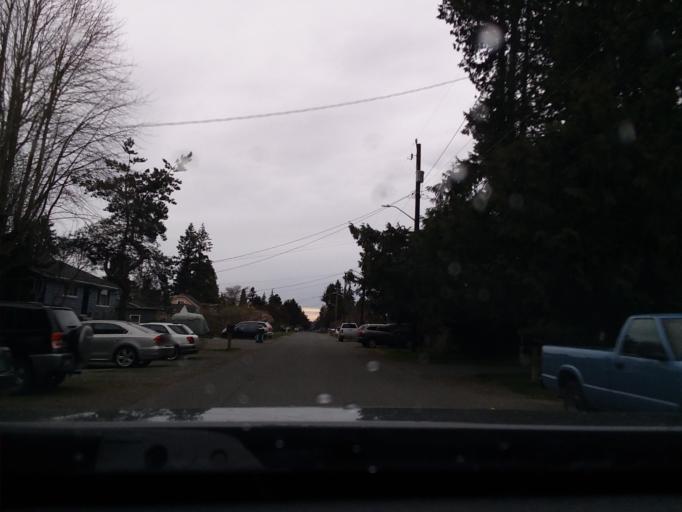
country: US
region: Washington
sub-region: King County
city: Shoreline
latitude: 47.6991
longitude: -122.3741
